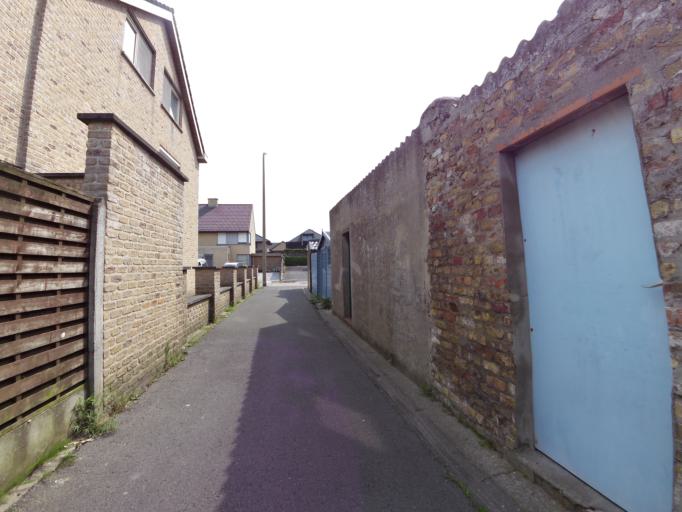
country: BE
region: Flanders
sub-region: Provincie West-Vlaanderen
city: Bredene
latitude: 51.2219
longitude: 2.9604
